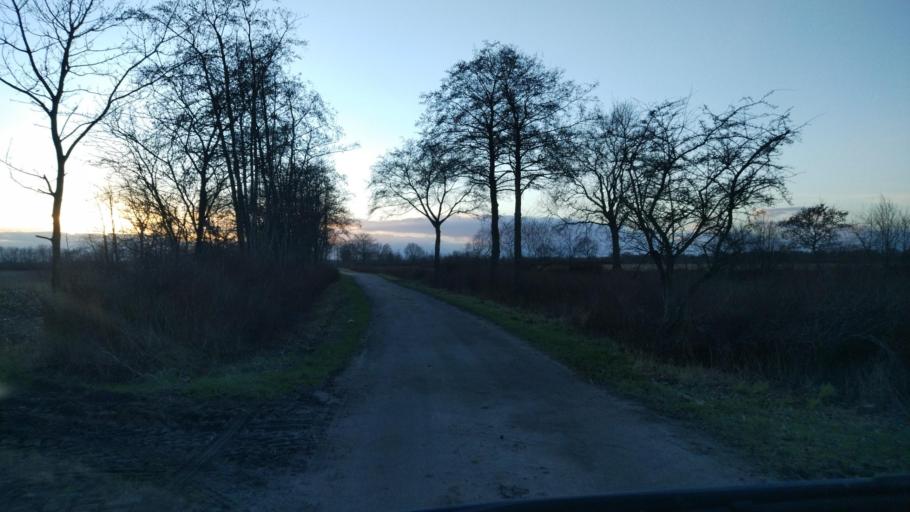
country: DE
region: Schleswig-Holstein
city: Gross Rheide
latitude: 54.4420
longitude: 9.4081
